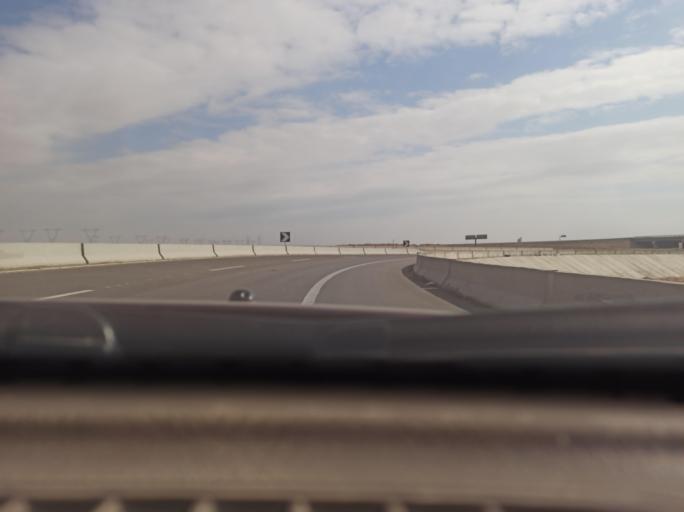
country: EG
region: Muhafazat al Fayyum
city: Tamiyah
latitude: 29.6444
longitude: 31.0129
